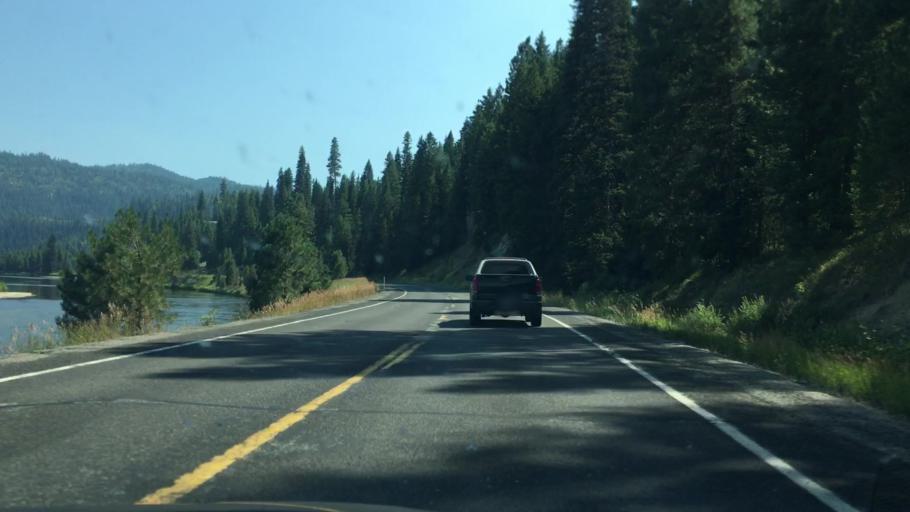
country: US
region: Idaho
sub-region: Valley County
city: Cascade
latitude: 44.2853
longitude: -116.0808
